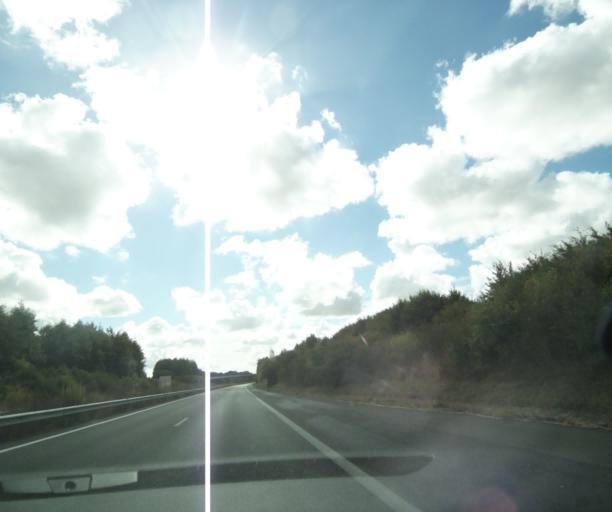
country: FR
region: Poitou-Charentes
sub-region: Departement de la Charente-Maritime
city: Cabariot
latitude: 45.9387
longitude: -0.8442
